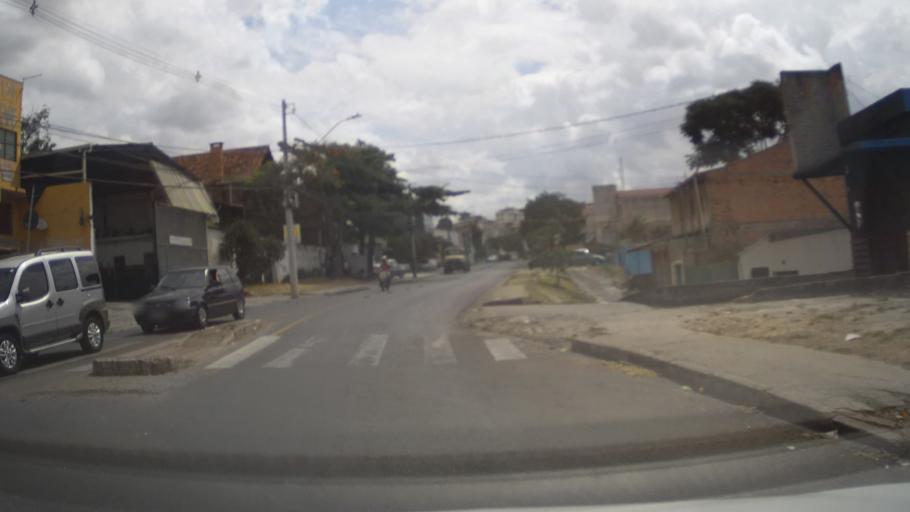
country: BR
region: Minas Gerais
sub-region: Belo Horizonte
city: Belo Horizonte
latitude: -19.8358
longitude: -43.9422
